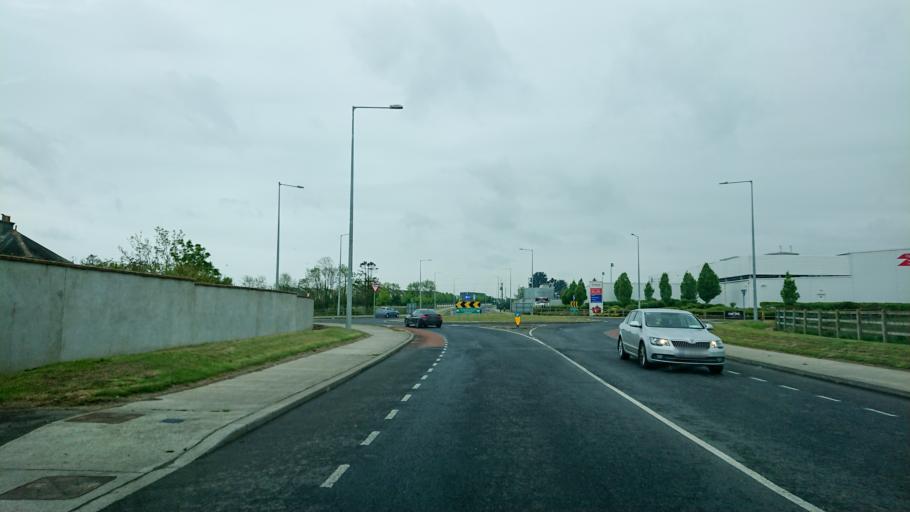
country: IE
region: Munster
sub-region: Waterford
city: Waterford
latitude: 52.2379
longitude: -7.1379
